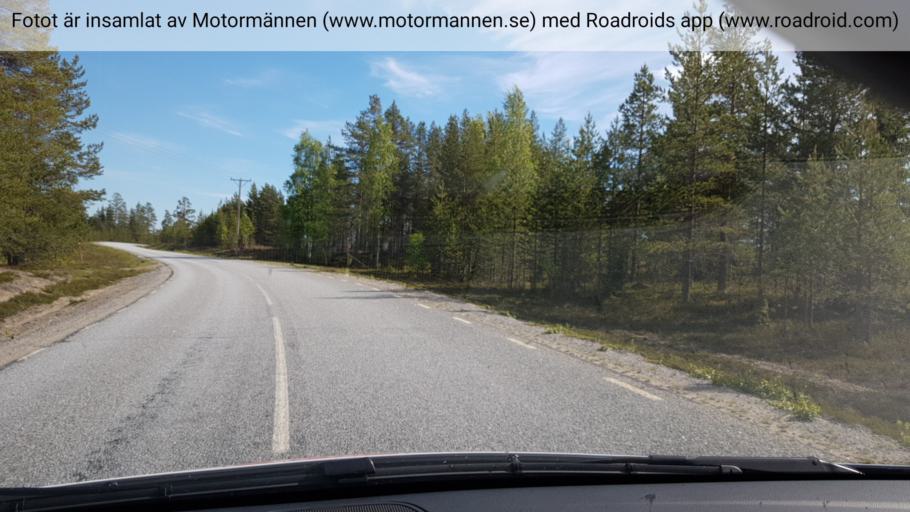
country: SE
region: Vaesterbotten
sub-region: Umea Kommun
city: Saevar
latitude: 63.9379
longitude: 20.5251
